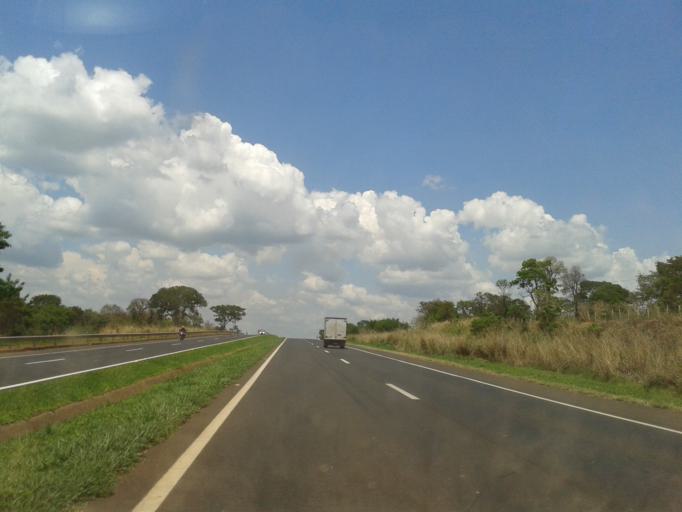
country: BR
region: Minas Gerais
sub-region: Araguari
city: Araguari
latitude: -18.7101
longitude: -48.1945
